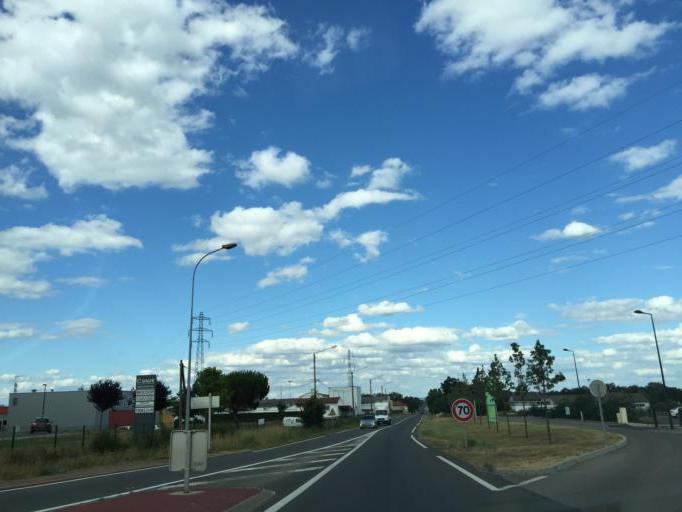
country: FR
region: Rhone-Alpes
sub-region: Departement de la Loire
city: Savigneux
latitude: 45.6101
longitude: 4.0964
